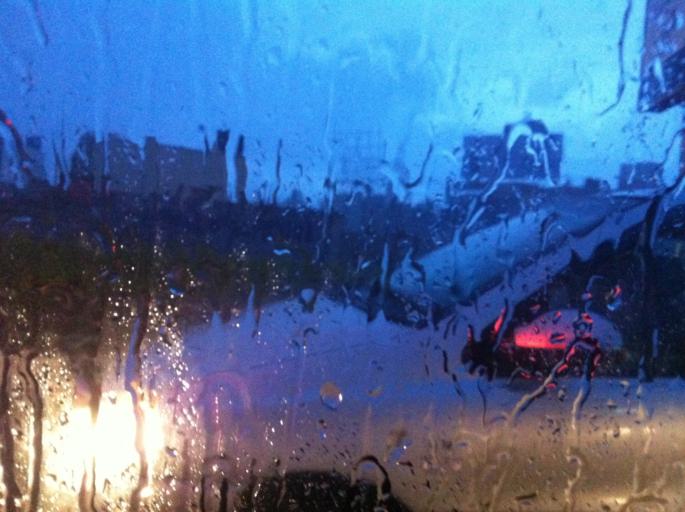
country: IN
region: Tamil Nadu
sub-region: Kancheepuram
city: Perungudi
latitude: 12.9778
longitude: 80.2518
